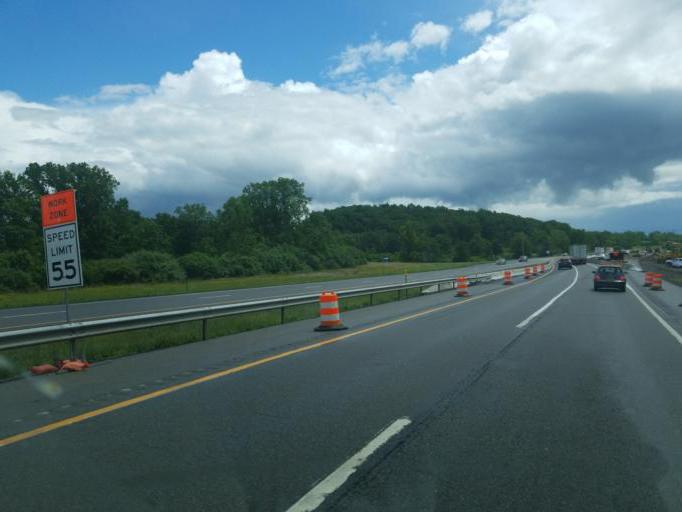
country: US
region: New York
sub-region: Ontario County
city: Victor
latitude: 43.0119
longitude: -77.4482
